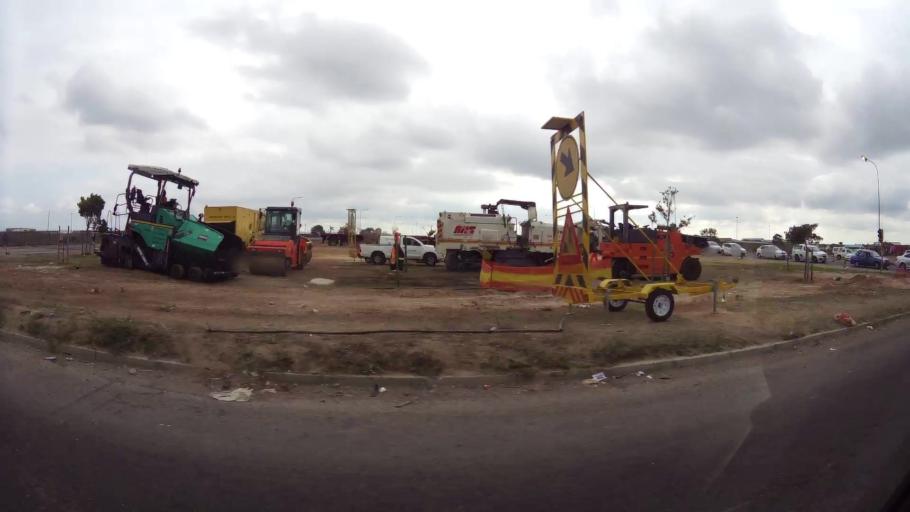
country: ZA
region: Eastern Cape
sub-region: Nelson Mandela Bay Metropolitan Municipality
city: Port Elizabeth
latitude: -33.8853
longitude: 25.5610
